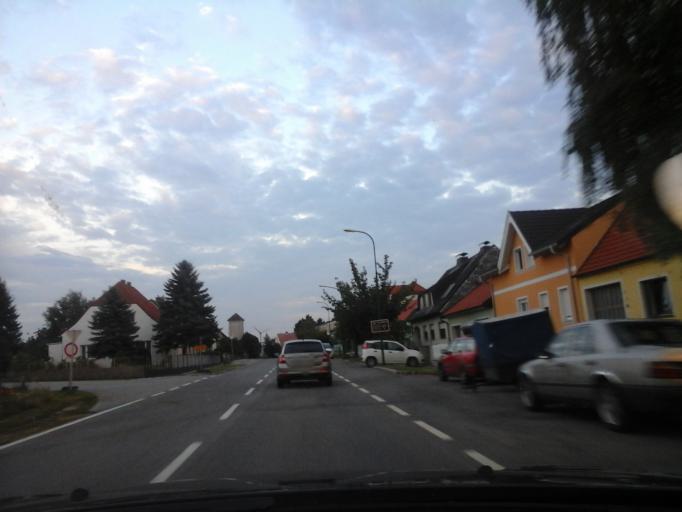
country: AT
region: Lower Austria
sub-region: Politischer Bezirk Bruck an der Leitha
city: Scharndorf
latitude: 48.0973
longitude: 16.7933
